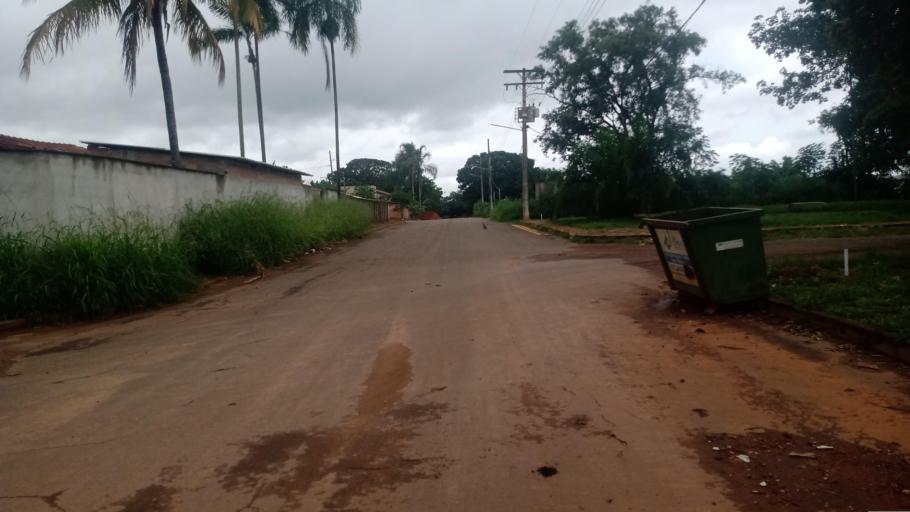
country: BR
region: Goias
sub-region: Senador Canedo
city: Senador Canedo
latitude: -16.7211
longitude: -49.1178
